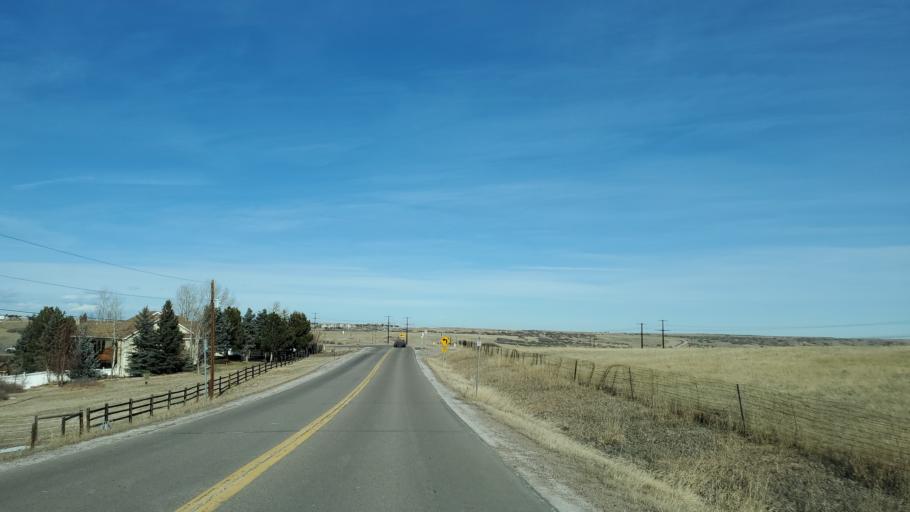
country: US
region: Colorado
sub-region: Douglas County
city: Castle Pines
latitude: 39.4484
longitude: -104.8725
